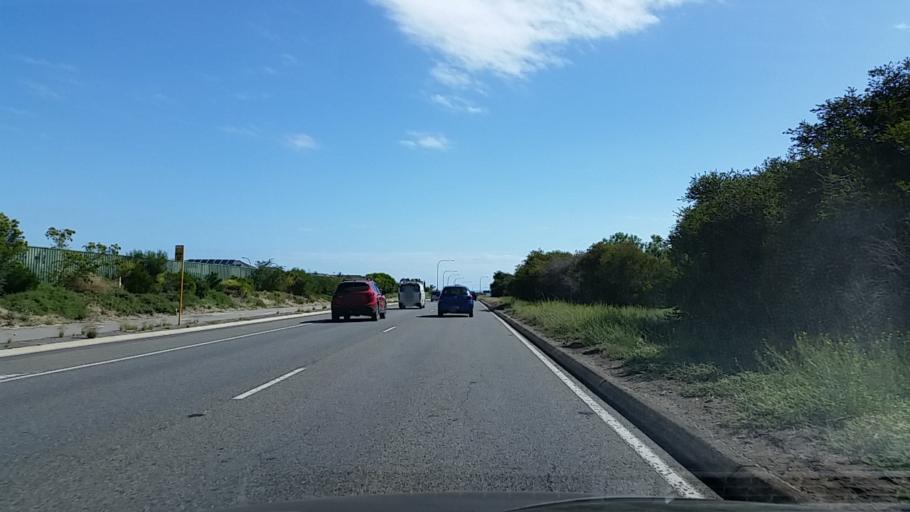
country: AU
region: South Australia
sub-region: Marion
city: Happy Valley
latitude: -35.0816
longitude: 138.5135
